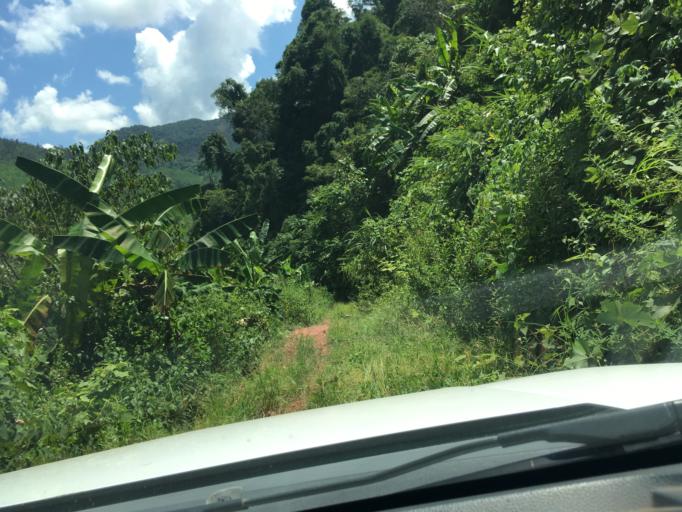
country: LA
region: Phongsali
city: Phongsali
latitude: 21.7917
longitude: 101.8634
